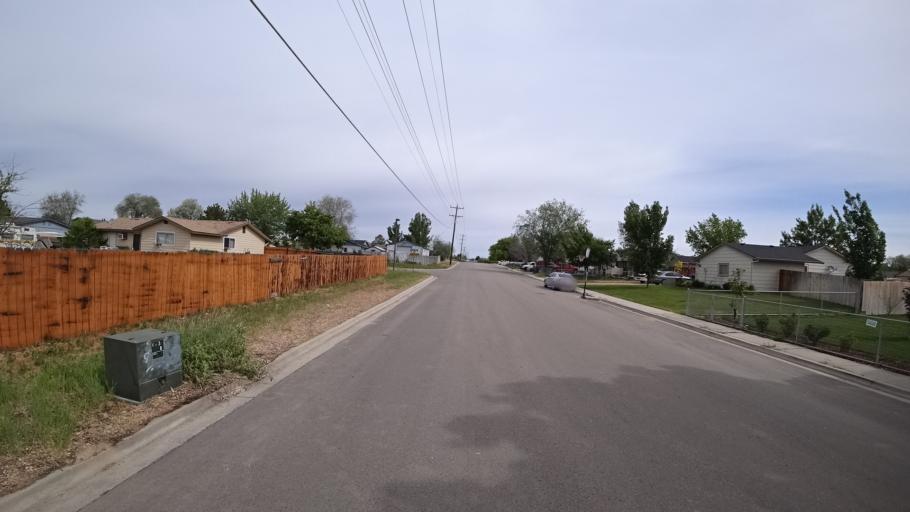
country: US
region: Idaho
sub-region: Ada County
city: Kuna
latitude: 43.5297
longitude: -116.3146
